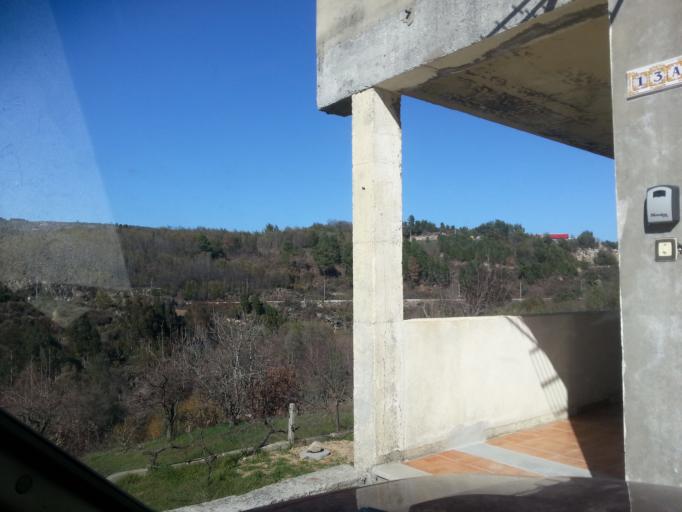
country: PT
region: Guarda
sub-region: Fornos de Algodres
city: Fornos de Algodres
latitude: 40.6137
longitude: -7.5148
